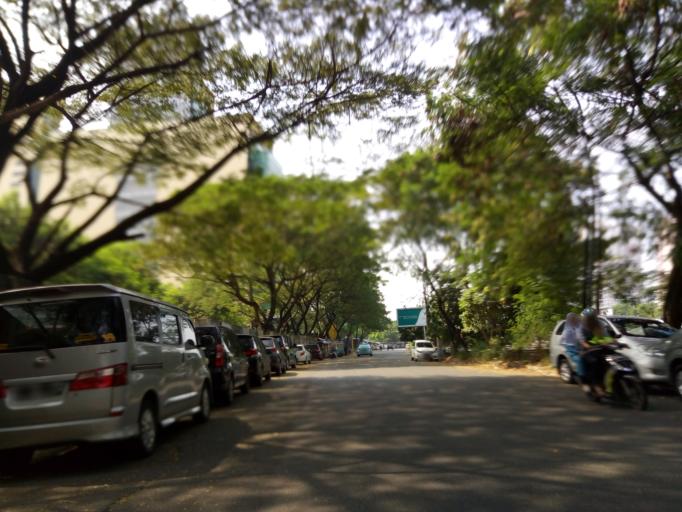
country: ID
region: Jakarta Raya
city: Jakarta
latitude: -6.2126
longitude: 106.8341
